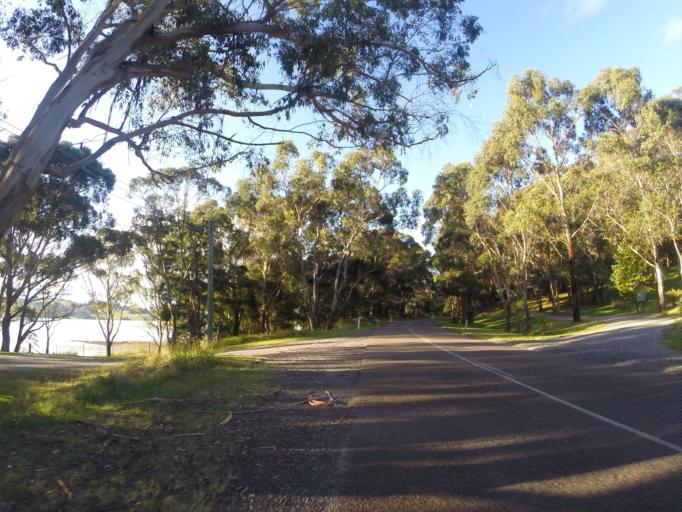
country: AU
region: New South Wales
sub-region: Shoalhaven Shire
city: Kangaroo Valley
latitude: -34.6488
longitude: 150.5051
